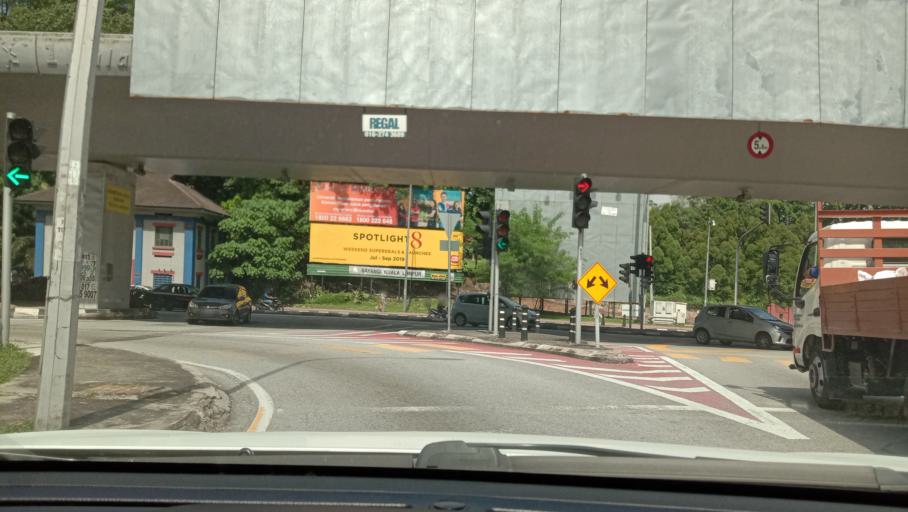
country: MY
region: Kuala Lumpur
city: Kuala Lumpur
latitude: 3.1317
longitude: 101.6827
